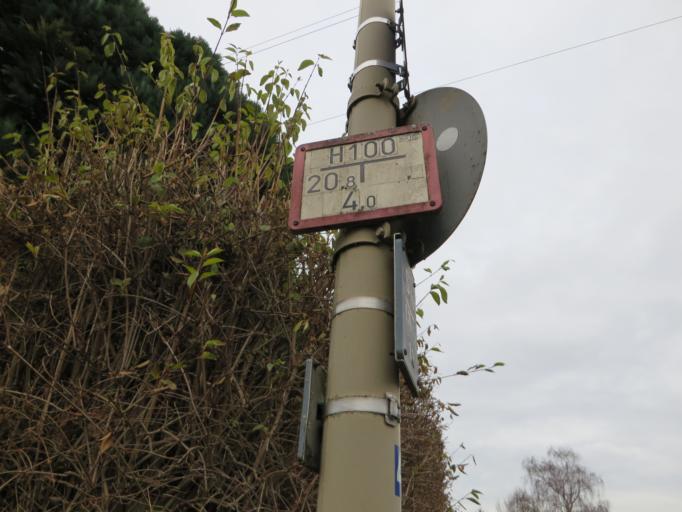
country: DE
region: North Rhine-Westphalia
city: Witten
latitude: 51.4372
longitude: 7.3189
